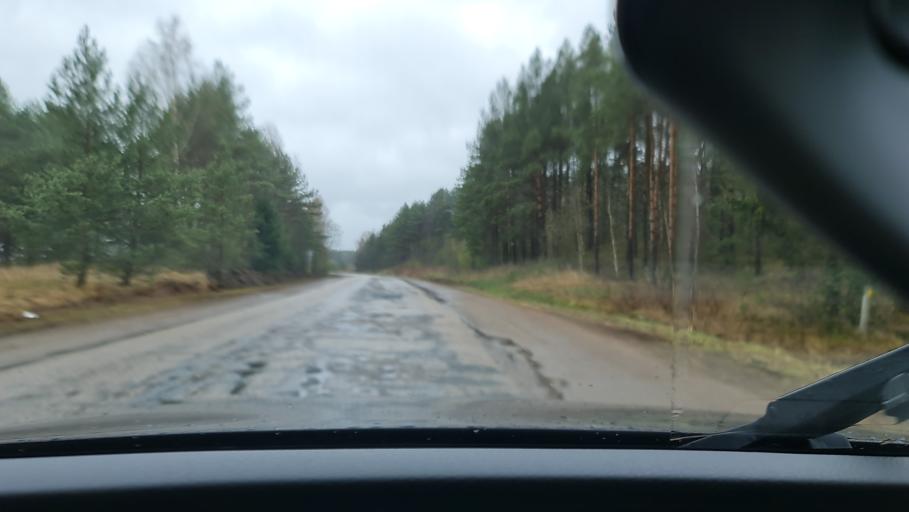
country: RU
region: Novgorod
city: Valday
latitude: 58.0400
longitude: 32.9266
